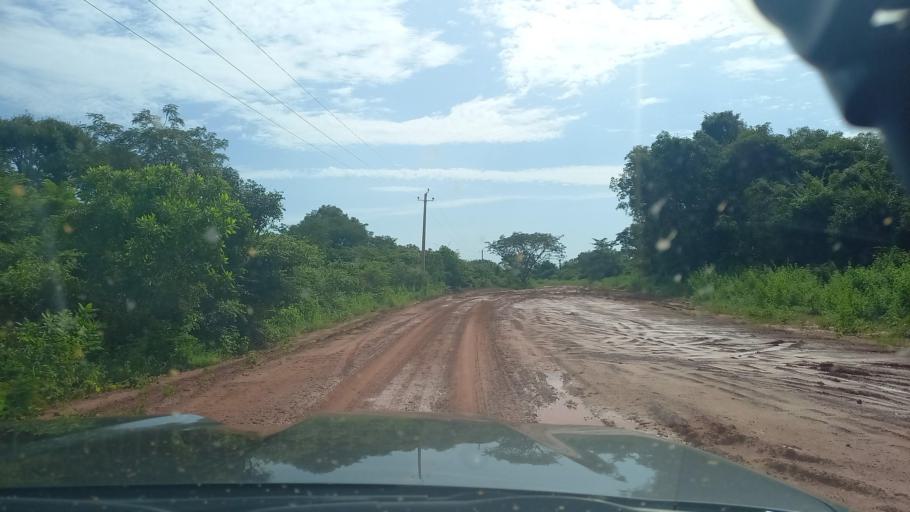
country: SN
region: Ziguinchor
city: Ziguinchor
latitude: 12.6718
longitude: -16.2170
